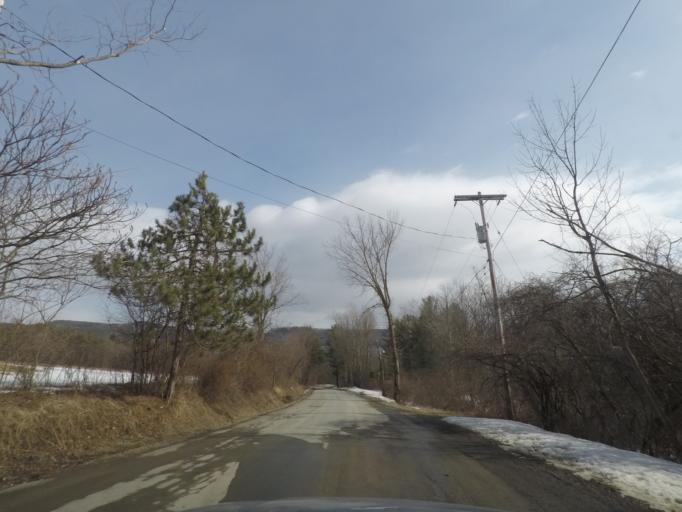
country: US
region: New York
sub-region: Rensselaer County
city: Poestenkill
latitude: 42.7766
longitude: -73.5533
